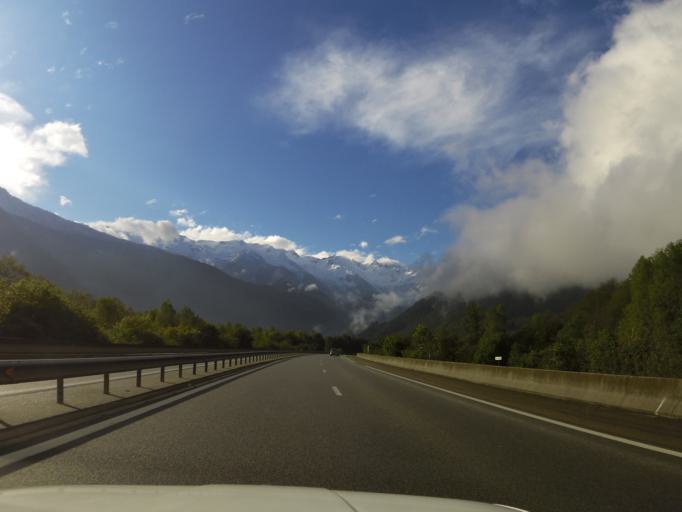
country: FR
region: Rhone-Alpes
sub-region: Departement de la Savoie
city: Aiton
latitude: 45.5544
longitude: 6.2900
